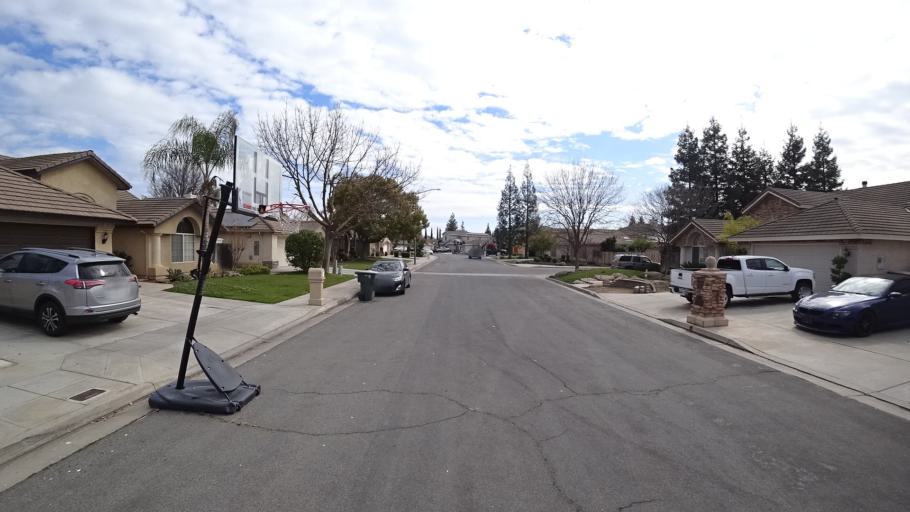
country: US
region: California
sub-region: Madera County
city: Bonadelle Ranchos-Madera Ranchos
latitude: 36.8461
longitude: -119.8844
